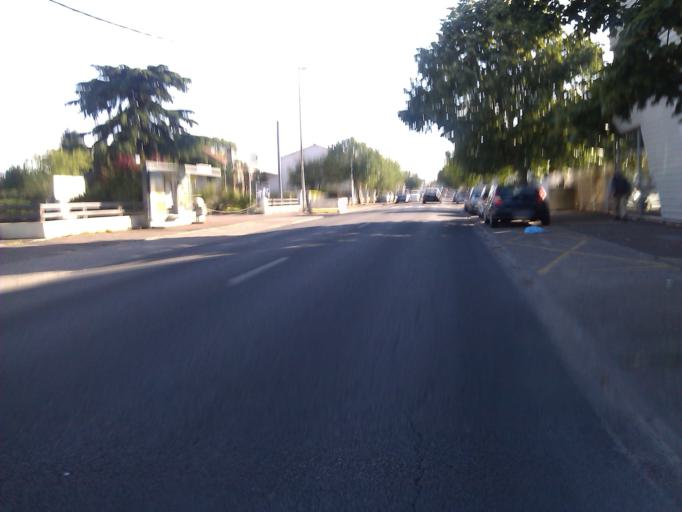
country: FR
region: Aquitaine
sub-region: Departement de la Gironde
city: Pessac
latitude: 44.8094
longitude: -0.6229
